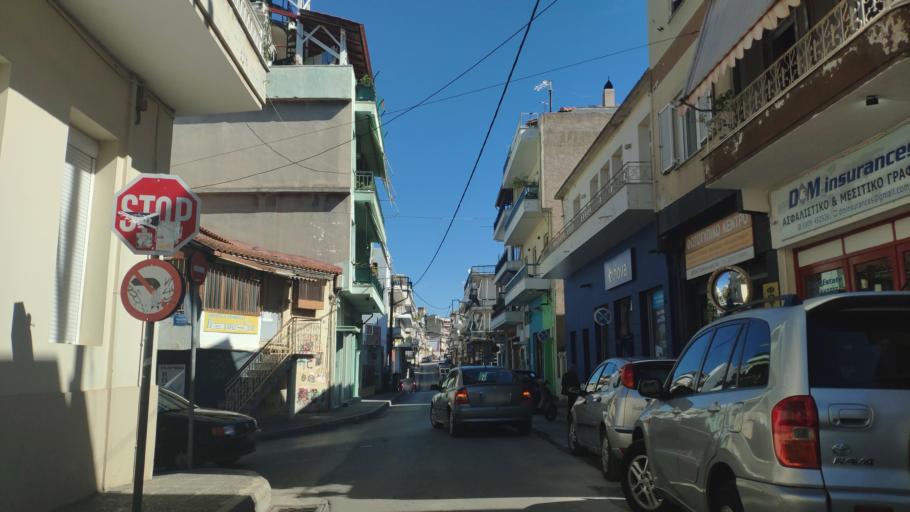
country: GR
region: Central Greece
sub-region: Nomos Voiotias
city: Livadeia
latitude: 38.4372
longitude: 22.8779
